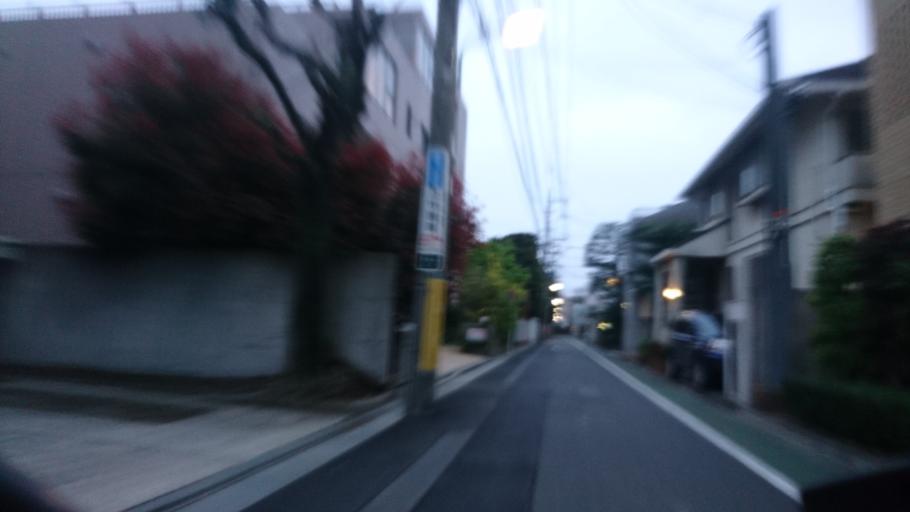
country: JP
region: Tokyo
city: Tokyo
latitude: 35.6219
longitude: 139.7355
